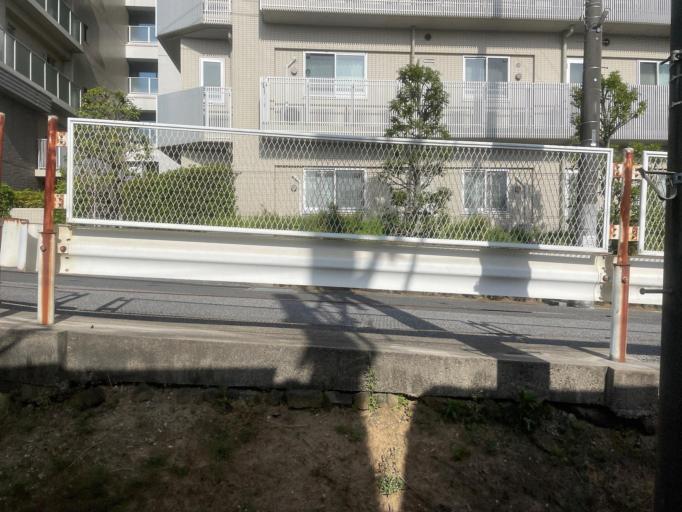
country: JP
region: Chiba
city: Nagareyama
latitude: 35.8543
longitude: 139.9018
